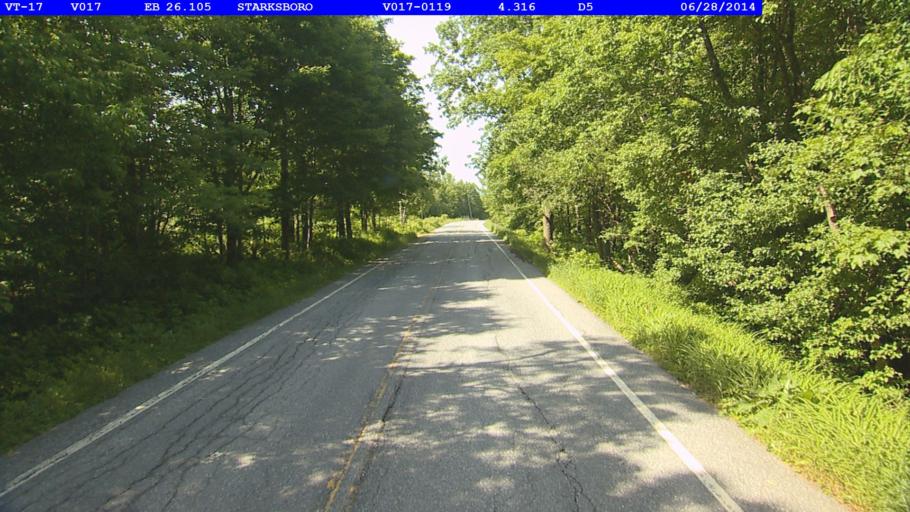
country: US
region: Vermont
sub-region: Addison County
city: Bristol
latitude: 44.2013
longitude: -72.9650
